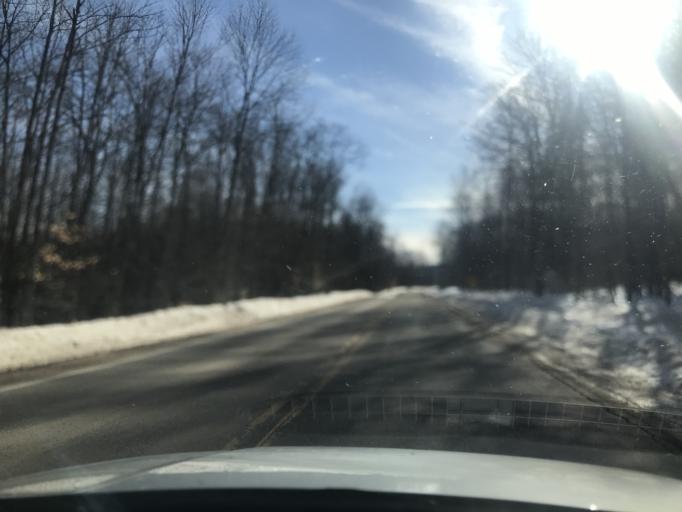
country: US
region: Michigan
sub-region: Dickinson County
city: Kingsford
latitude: 45.4175
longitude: -88.3965
